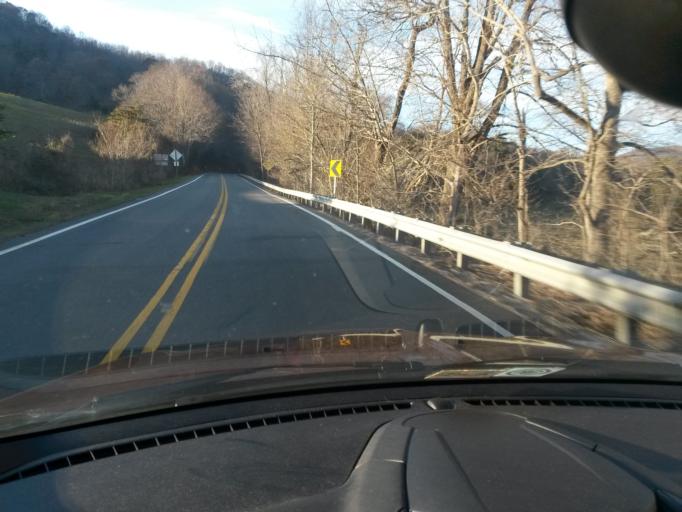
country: US
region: Virginia
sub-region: City of Buena Vista
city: Buena Vista
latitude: 37.6912
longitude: -79.2412
